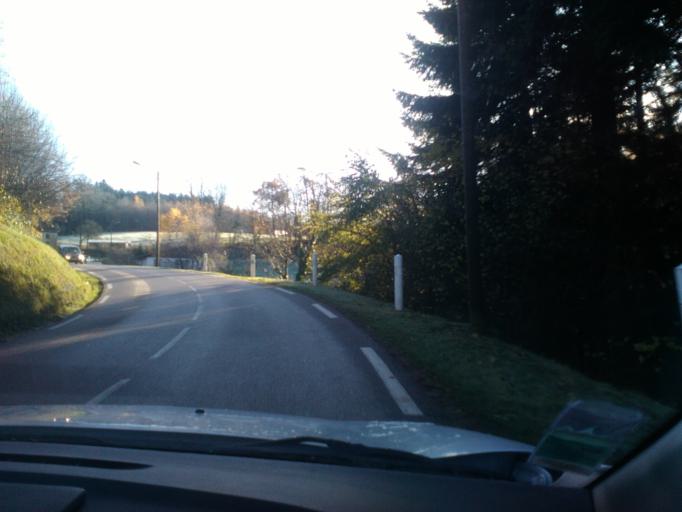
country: FR
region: Lorraine
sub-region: Departement des Vosges
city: Xertigny
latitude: 48.0421
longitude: 6.4110
